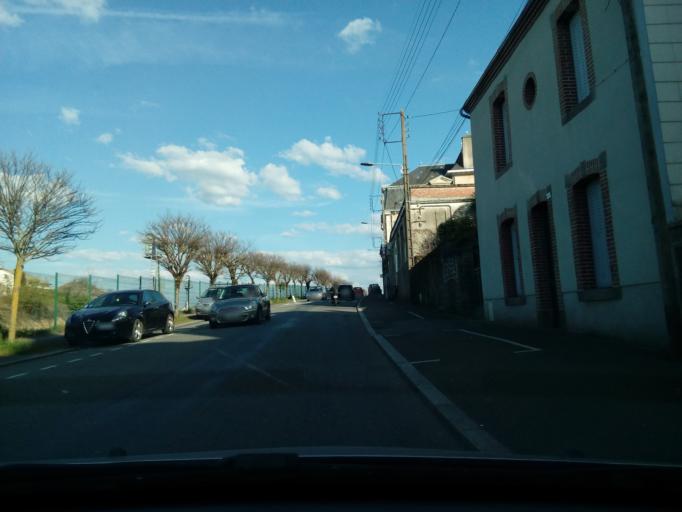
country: FR
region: Limousin
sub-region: Departement de la Creuse
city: Gueret
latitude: 46.1749
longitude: 1.8755
